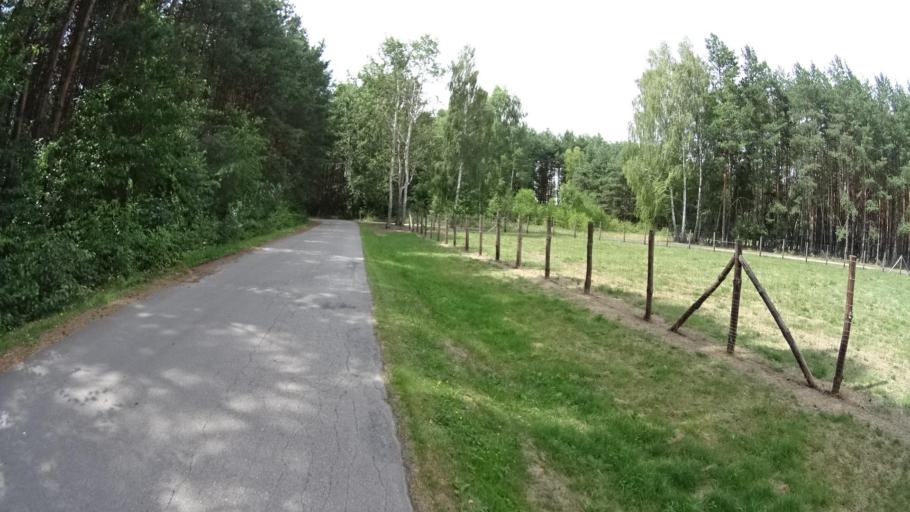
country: PL
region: Masovian Voivodeship
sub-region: Powiat bialobrzeski
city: Wysmierzyce
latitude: 51.6388
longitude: 20.8727
